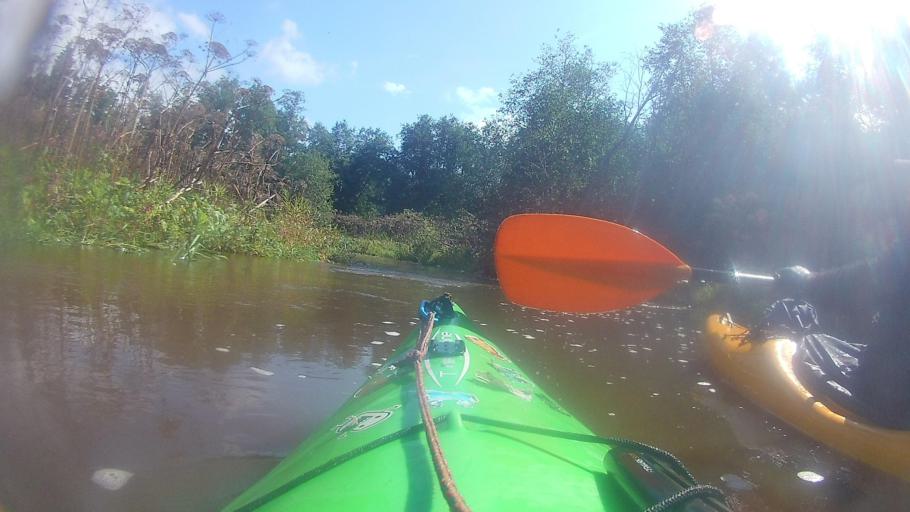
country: LV
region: Talsu Rajons
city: Sabile
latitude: 57.0004
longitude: 22.6030
